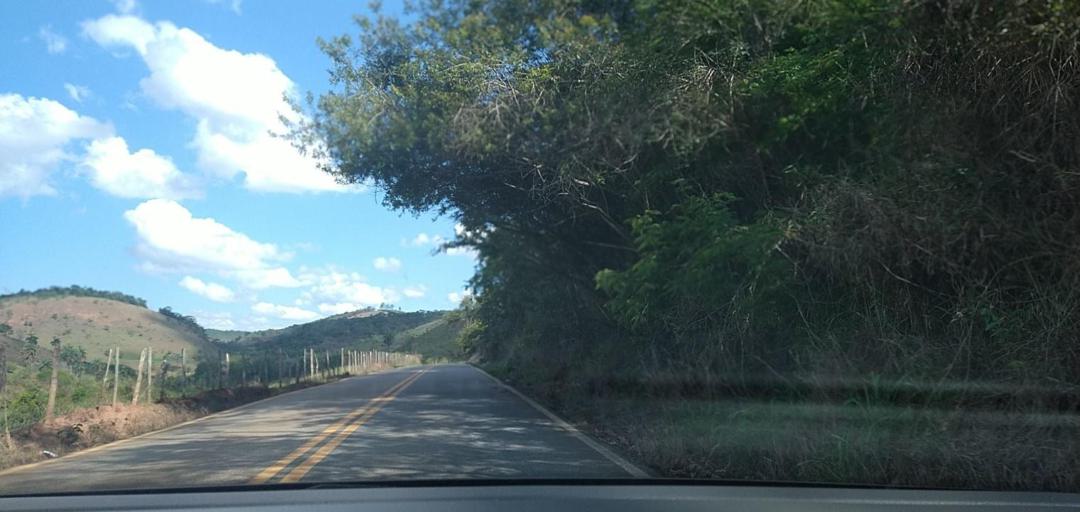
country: BR
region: Minas Gerais
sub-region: Rio Piracicaba
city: Rio Piracicaba
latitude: -19.9895
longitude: -43.1200
